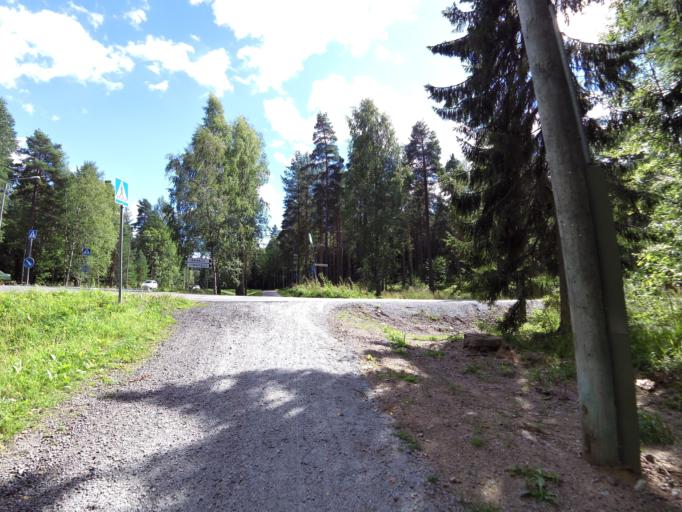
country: FI
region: Pirkanmaa
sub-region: Tampere
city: Yloejaervi
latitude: 61.5119
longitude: 23.6183
